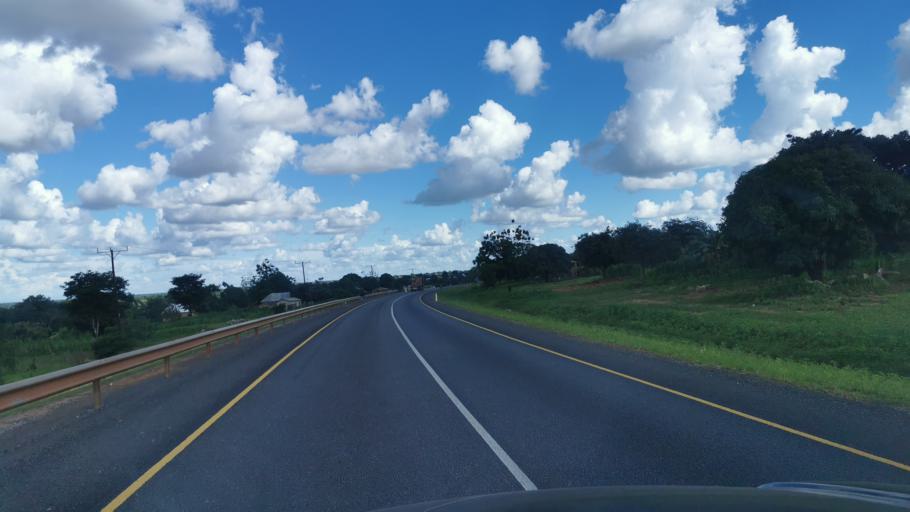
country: TZ
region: Geita
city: Ushirombo
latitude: -3.4354
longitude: 31.8325
